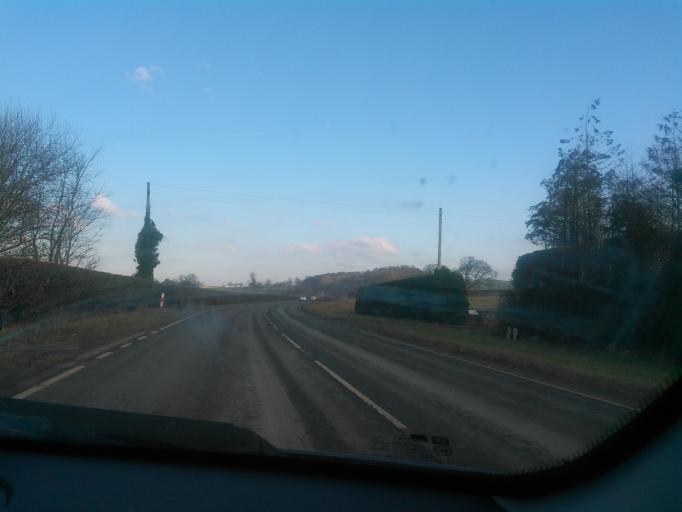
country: GB
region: England
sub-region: Shropshire
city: Wem
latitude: 52.8306
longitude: -2.6808
